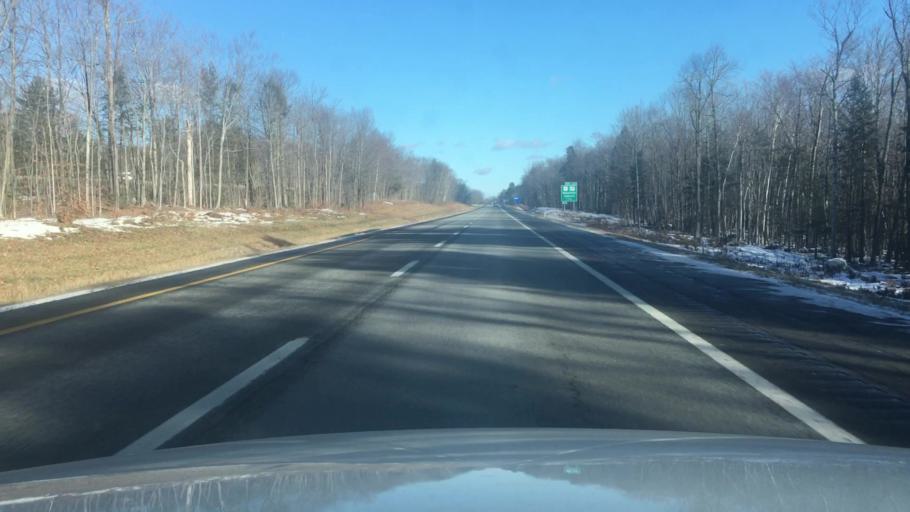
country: US
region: Maine
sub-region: Kennebec County
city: Oakland
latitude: 44.5312
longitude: -69.6903
